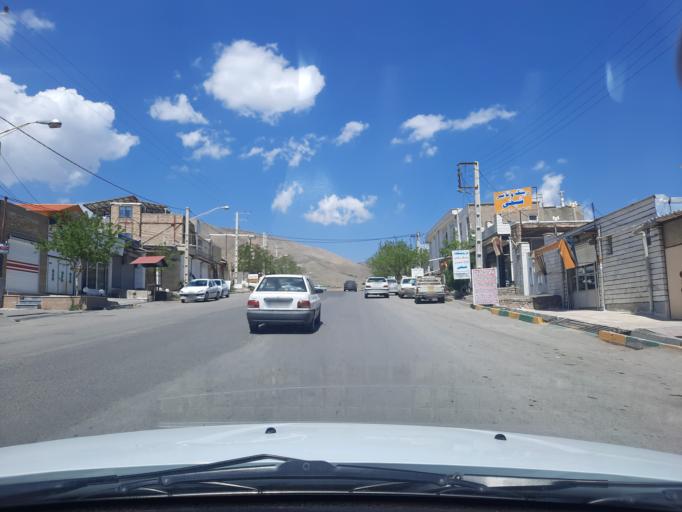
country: IR
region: Qazvin
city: Qazvin
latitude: 36.3337
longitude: 50.1519
